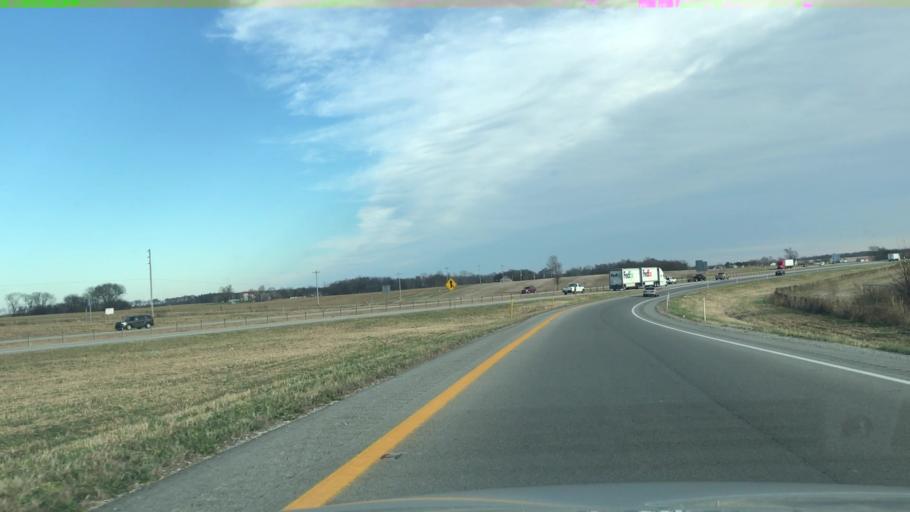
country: US
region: Kentucky
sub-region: Christian County
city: Oak Grove
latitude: 36.6803
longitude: -87.4027
